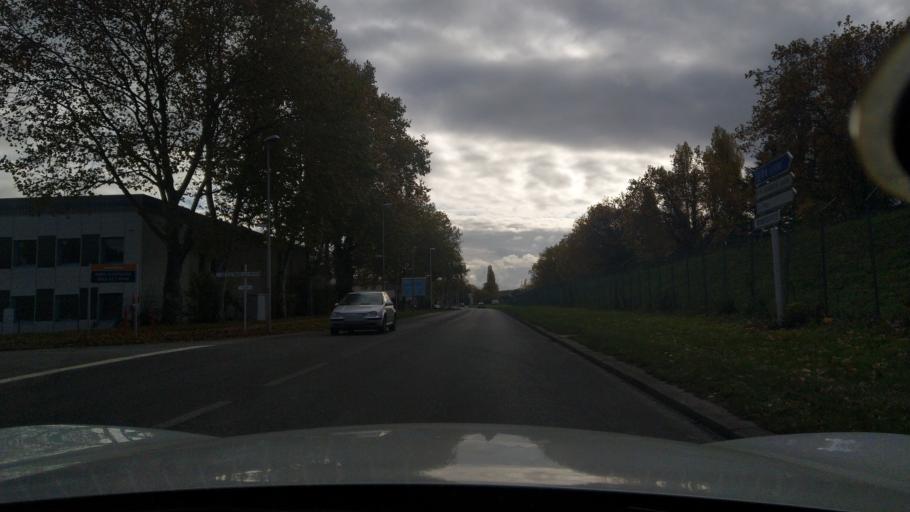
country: FR
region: Ile-de-France
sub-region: Departement de l'Essonne
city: Courcouronnes
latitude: 48.6323
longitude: 2.3960
